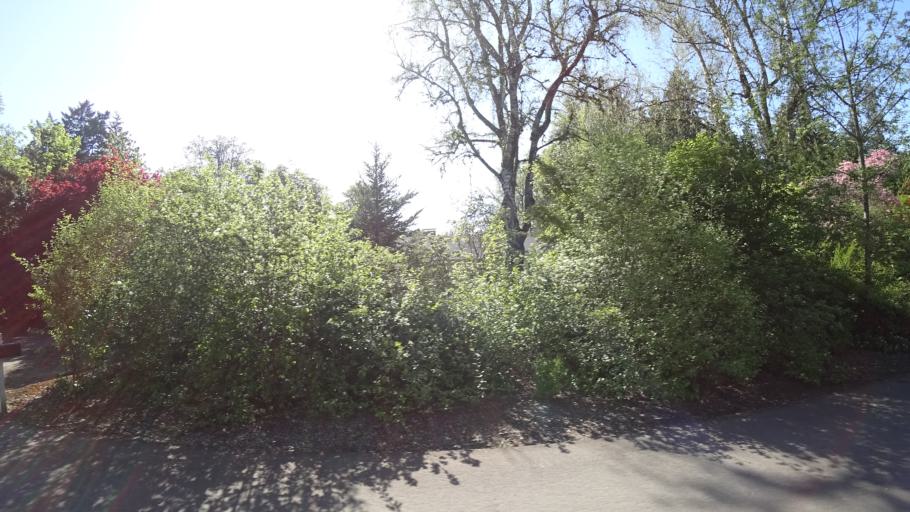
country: US
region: Oregon
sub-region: Washington County
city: Hillsboro
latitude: 45.5323
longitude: -122.9859
